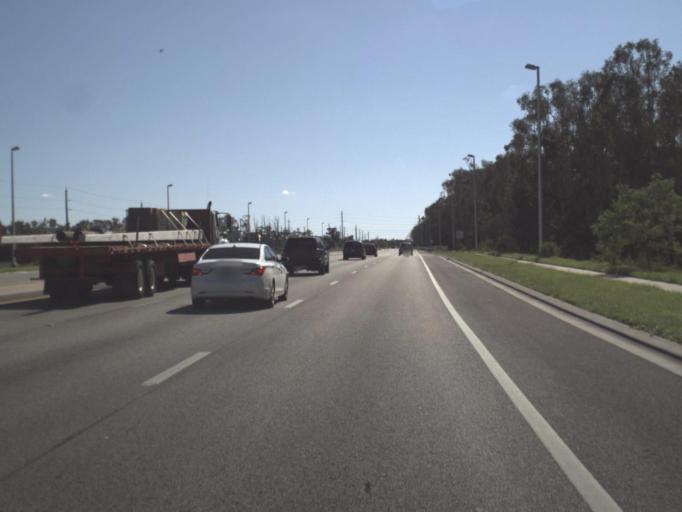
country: US
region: Florida
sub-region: Lee County
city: Tice
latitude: 26.6315
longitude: -81.7919
